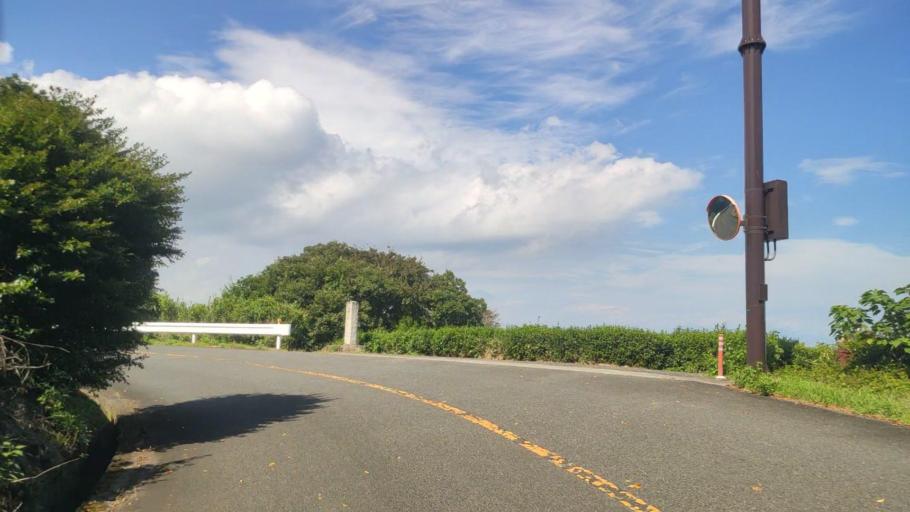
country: JP
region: Shizuoka
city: Shizuoka-shi
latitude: 34.9796
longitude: 138.4747
